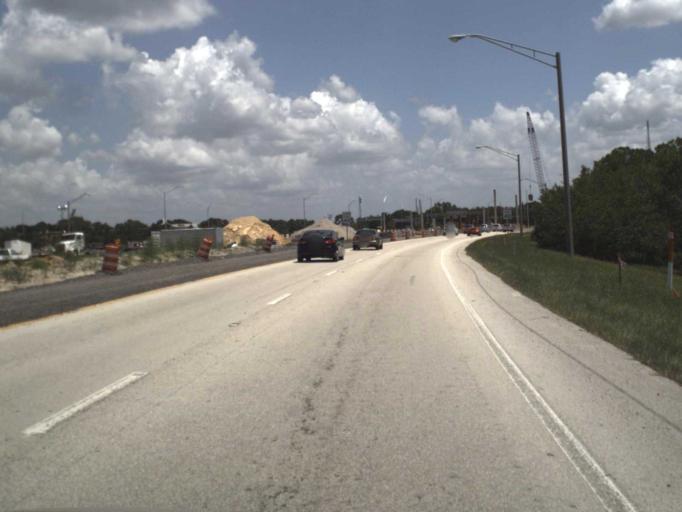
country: US
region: Florida
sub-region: Pinellas County
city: Gandy
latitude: 27.8635
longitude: -82.6438
